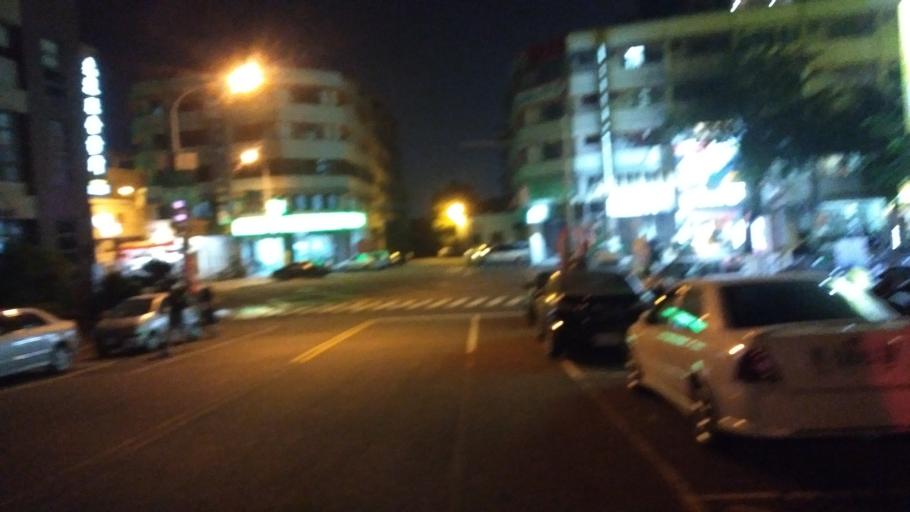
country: TW
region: Taiwan
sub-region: Taichung City
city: Taichung
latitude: 24.1860
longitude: 120.6096
